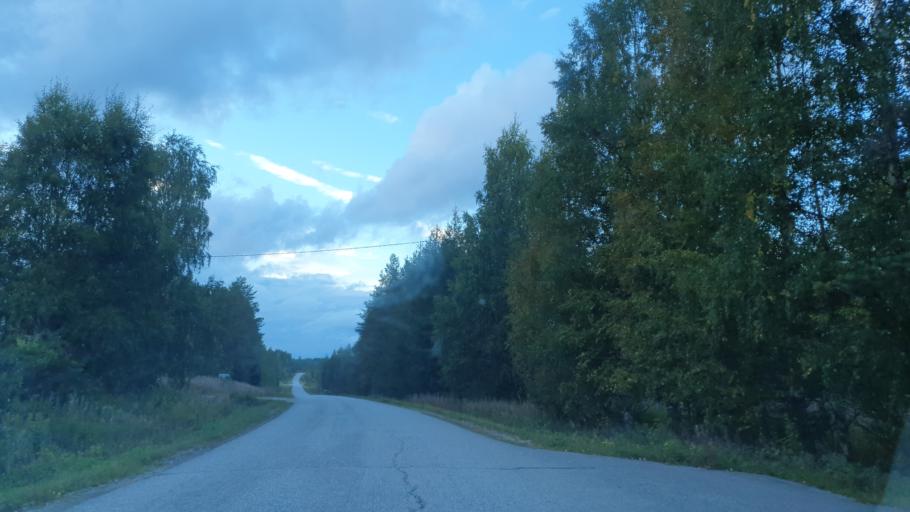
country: FI
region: Kainuu
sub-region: Kehys-Kainuu
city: Kuhmo
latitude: 64.3848
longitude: 29.8703
